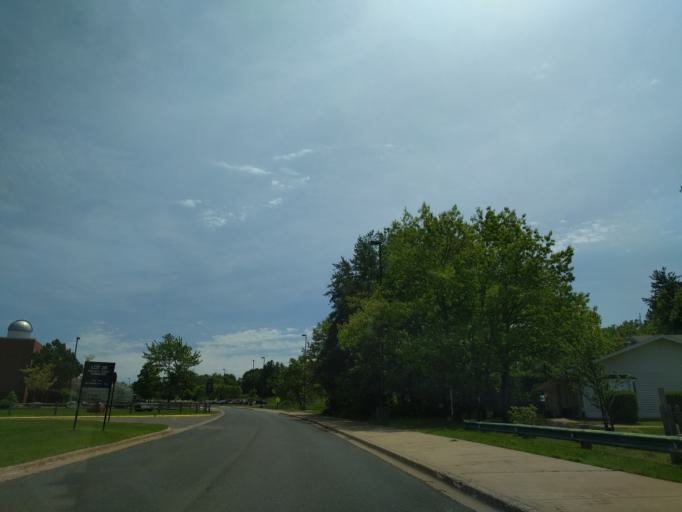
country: US
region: Michigan
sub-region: Marquette County
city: Marquette
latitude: 46.5597
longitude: -87.4099
